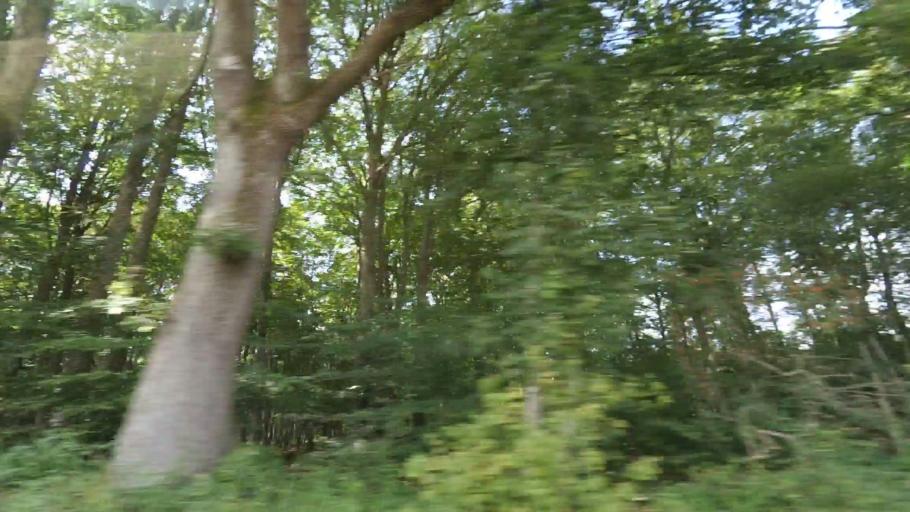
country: DK
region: Central Jutland
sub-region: Syddjurs Kommune
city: Ryomgard
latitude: 56.4648
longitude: 10.5221
